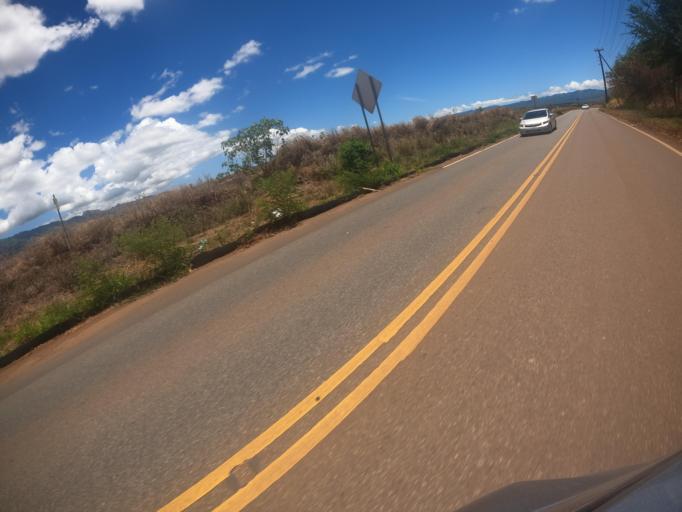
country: US
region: Hawaii
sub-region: Honolulu County
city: Royal Kunia
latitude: 21.3736
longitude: -158.0421
